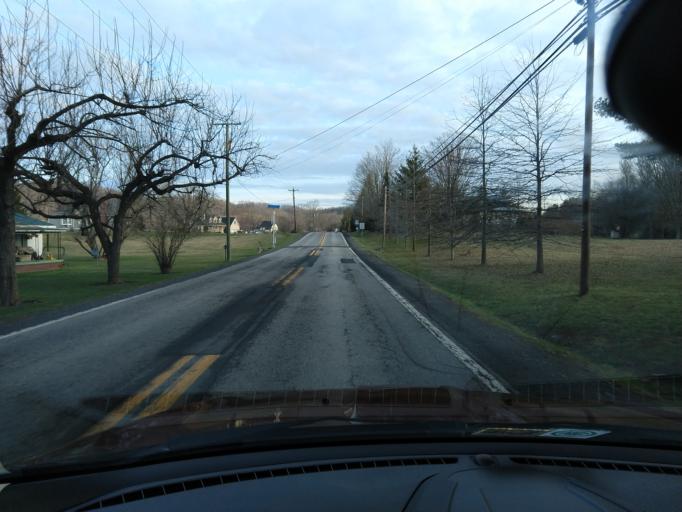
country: US
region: West Virginia
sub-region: Greenbrier County
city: Lewisburg
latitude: 37.9281
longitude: -80.3848
